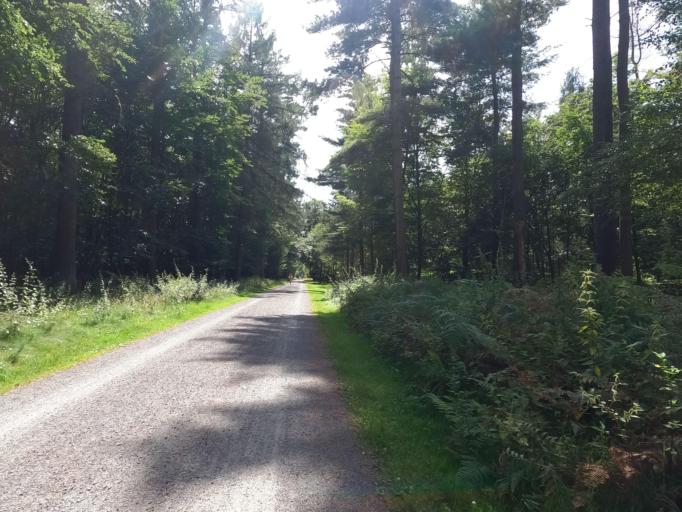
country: DE
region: Hesse
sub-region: Regierungsbezirk Darmstadt
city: Neu Isenburg
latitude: 50.0725
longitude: 8.7157
